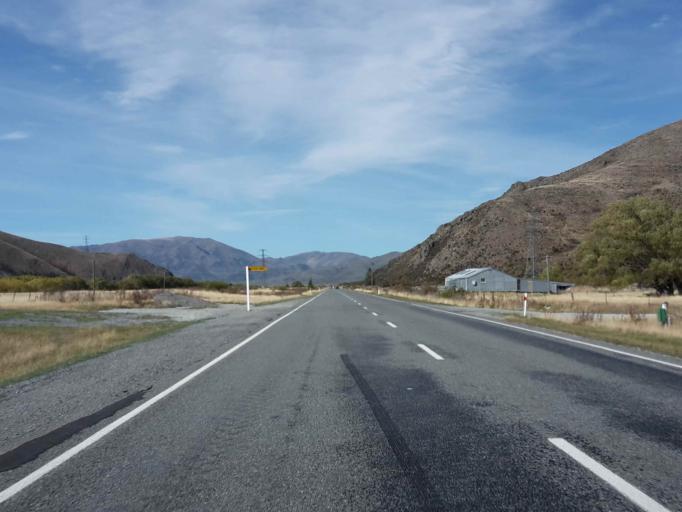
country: NZ
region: Otago
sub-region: Queenstown-Lakes District
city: Wanaka
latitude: -44.4996
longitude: 169.7642
